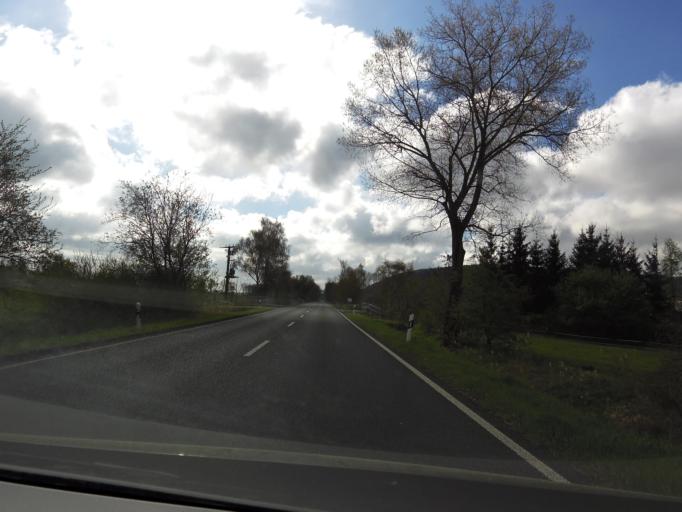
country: DE
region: Thuringia
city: Tuttleben
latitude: 50.9374
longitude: 10.7692
